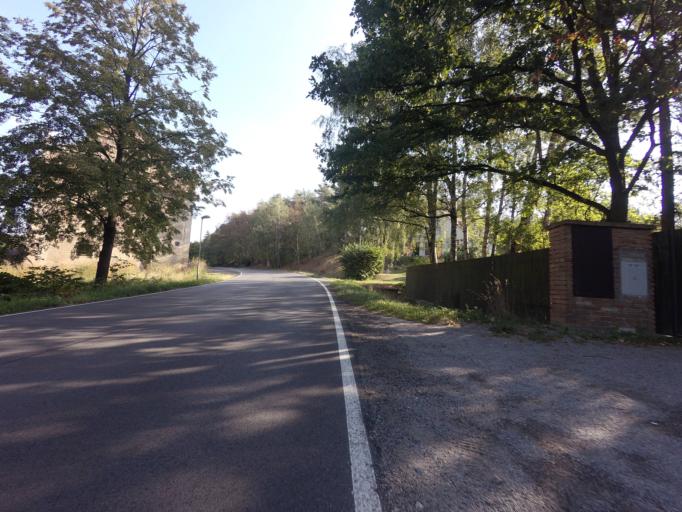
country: CZ
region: Jihocesky
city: Tyn nad Vltavou
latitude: 49.2486
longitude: 14.4209
